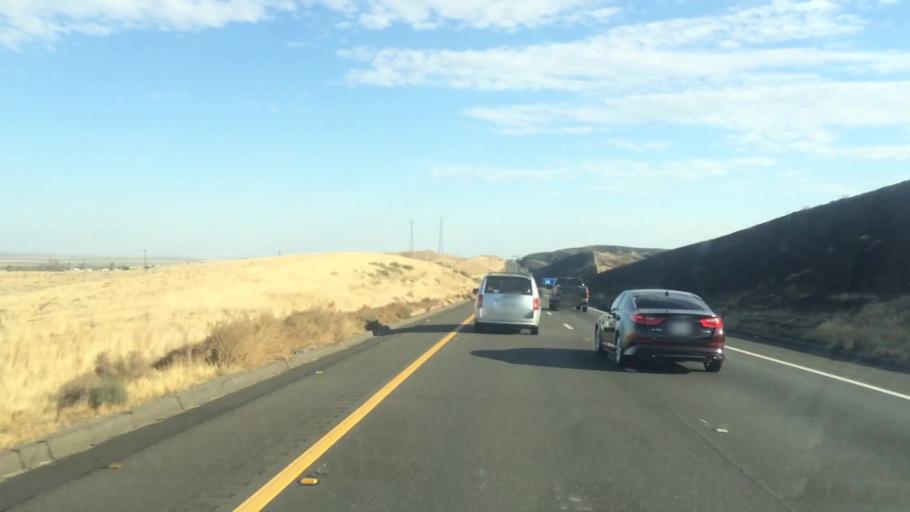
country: US
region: California
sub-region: Kings County
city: Kettleman City
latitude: 35.9950
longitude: -119.9742
